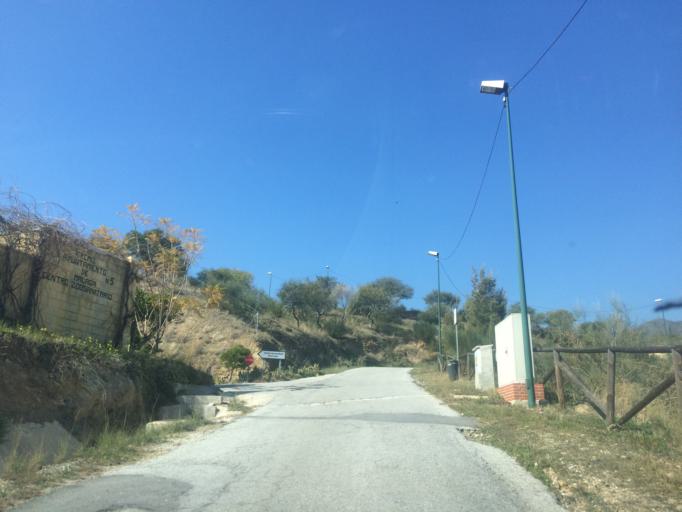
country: ES
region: Andalusia
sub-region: Provincia de Malaga
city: Malaga
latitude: 36.7524
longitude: -4.4358
